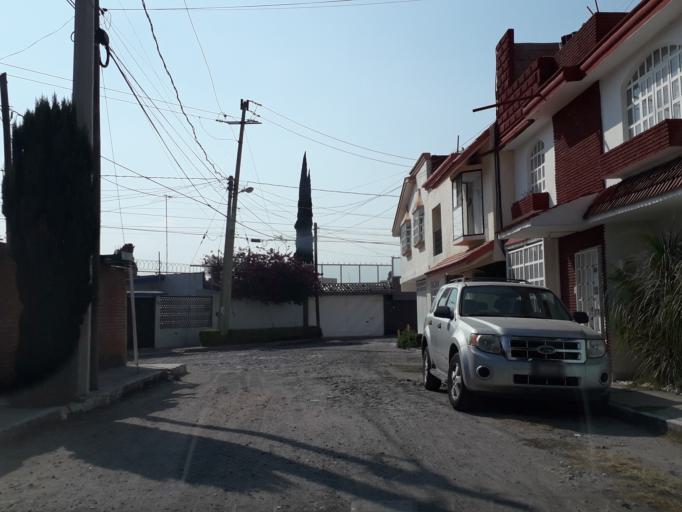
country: MX
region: Puebla
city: Puebla
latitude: 19.0137
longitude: -98.2115
